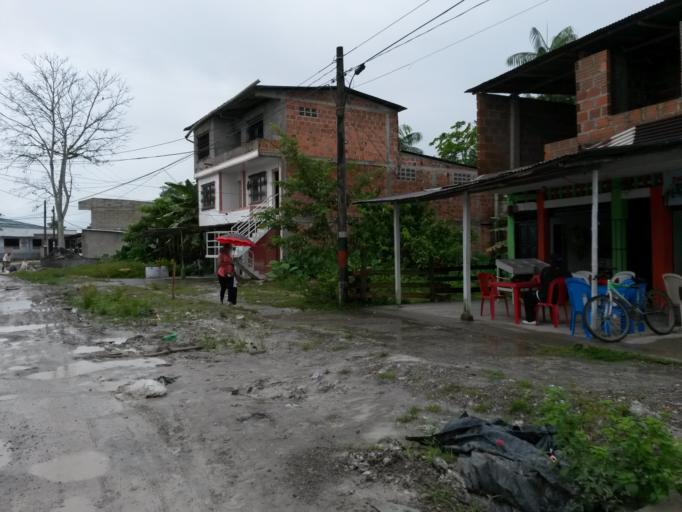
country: CO
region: Cauca
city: Guapi
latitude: 2.5723
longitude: -77.8906
